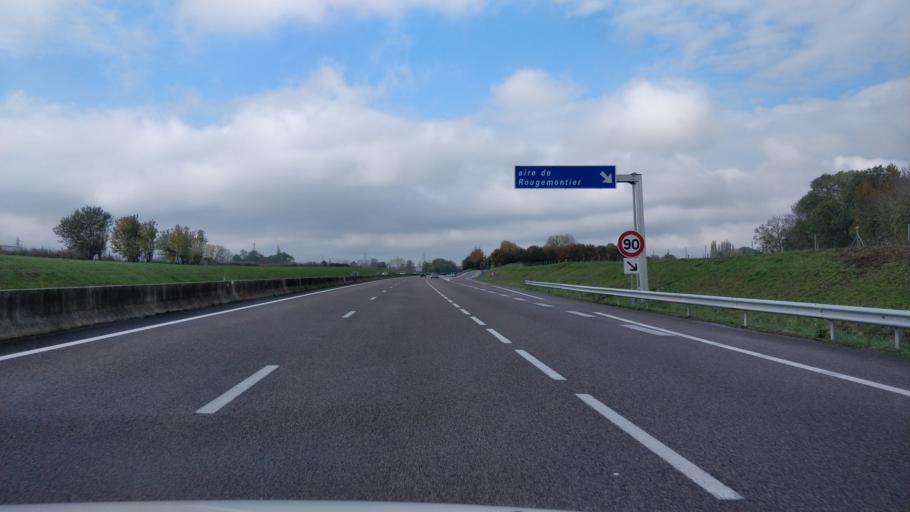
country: FR
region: Haute-Normandie
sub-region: Departement de l'Eure
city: Hauville
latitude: 49.3704
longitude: 0.7146
